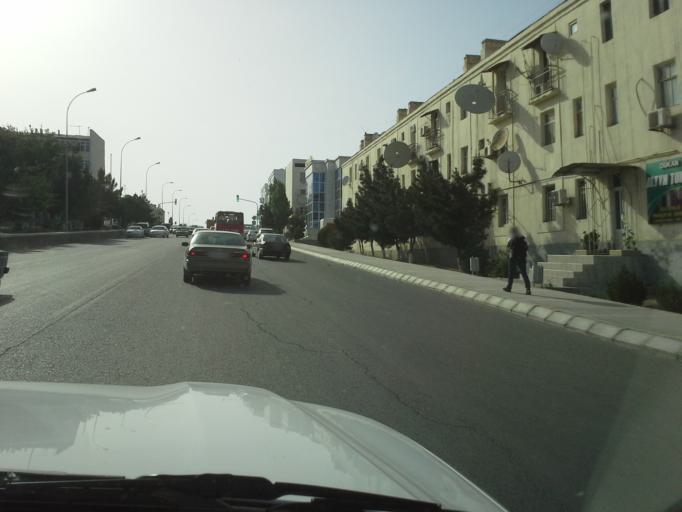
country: TM
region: Balkan
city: Turkmenbasy
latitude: 40.0164
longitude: 52.9784
